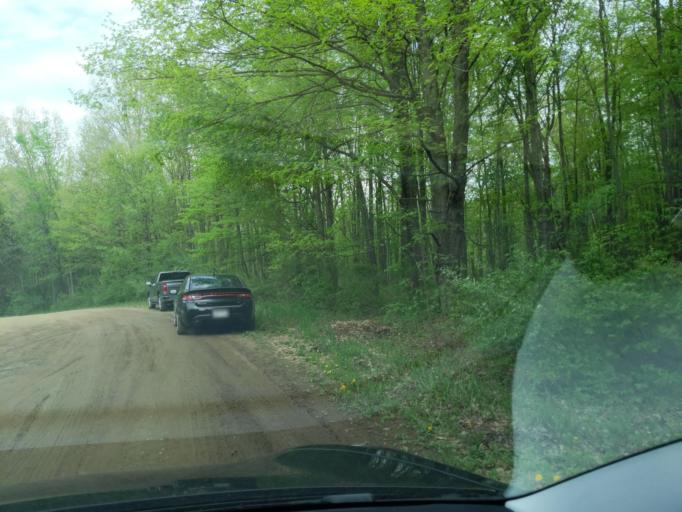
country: US
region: Michigan
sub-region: Washtenaw County
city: Chelsea
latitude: 42.4124
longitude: -84.0703
